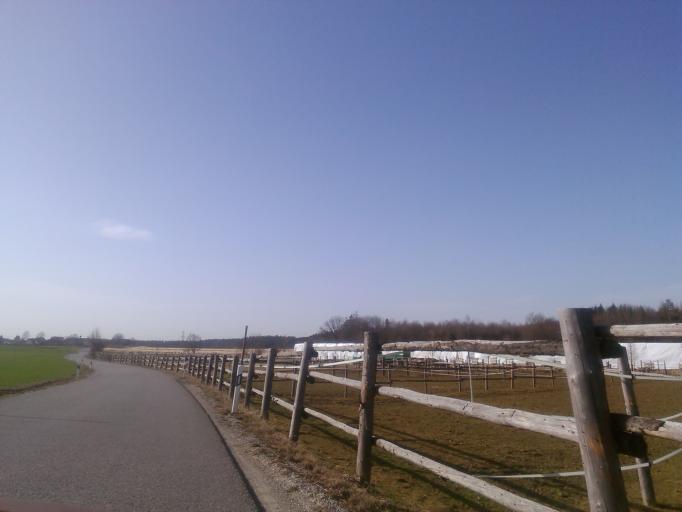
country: DE
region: Bavaria
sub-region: Upper Bavaria
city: Gauting
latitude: 48.0833
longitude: 11.3413
